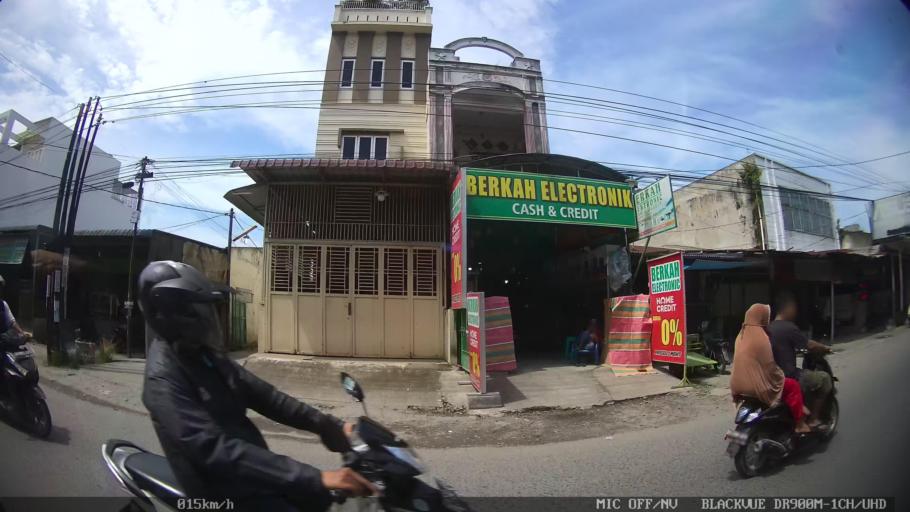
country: ID
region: North Sumatra
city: Labuhan Deli
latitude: 3.6876
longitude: 98.6645
